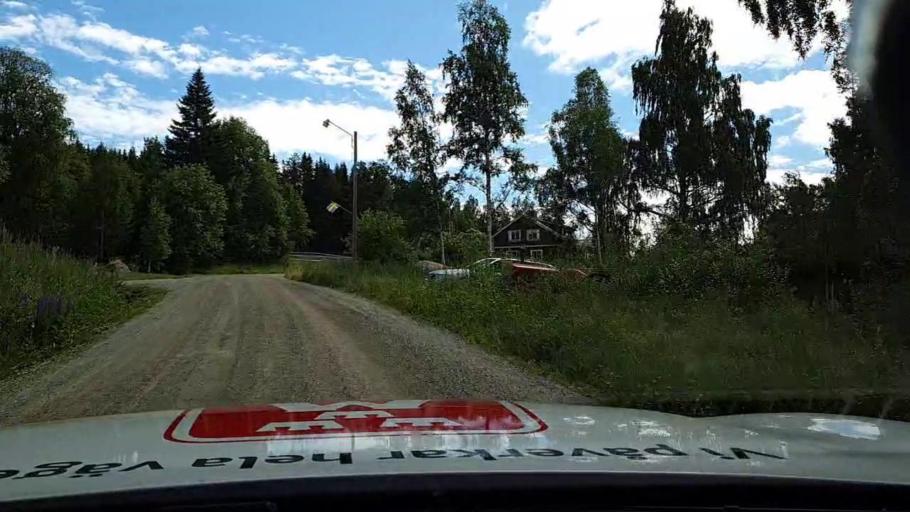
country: SE
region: Jaemtland
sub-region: Braecke Kommun
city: Braecke
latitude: 62.7691
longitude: 15.4881
